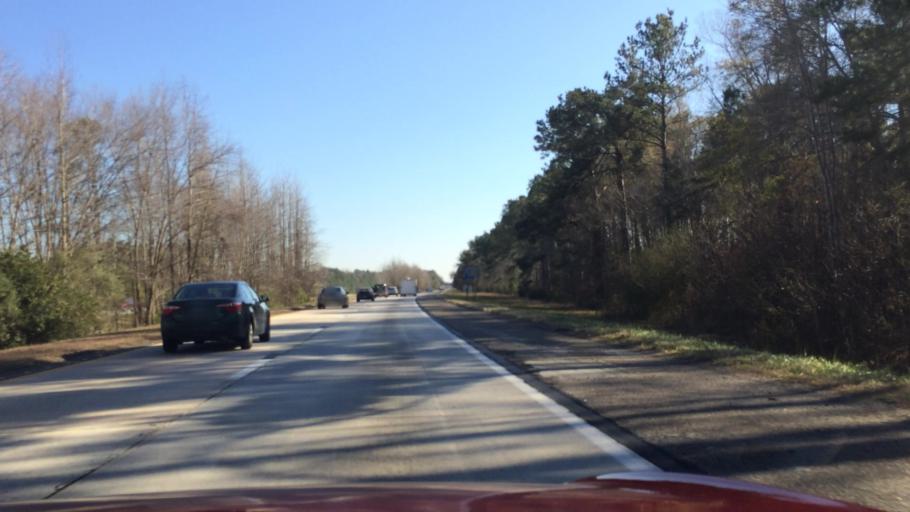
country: US
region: South Carolina
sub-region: Orangeburg County
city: Holly Hill
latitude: 33.2639
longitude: -80.4802
